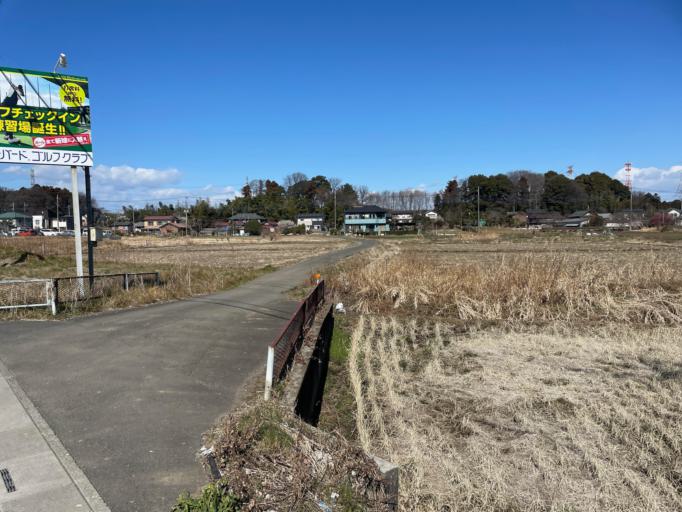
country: JP
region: Saitama
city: Sakado
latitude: 35.9524
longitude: 139.4371
